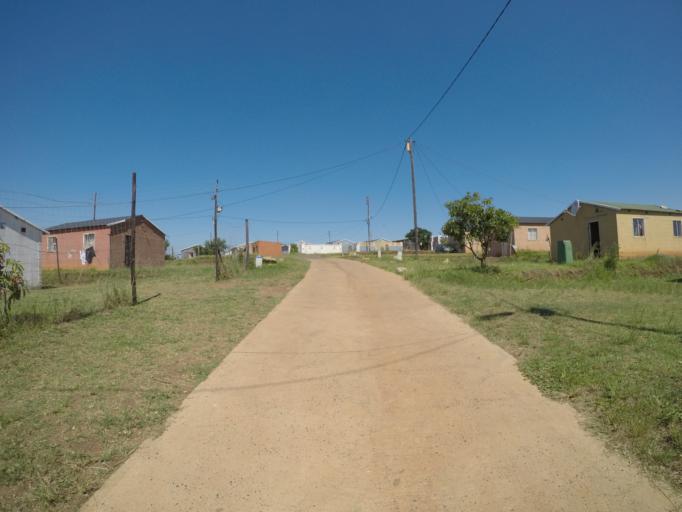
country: ZA
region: KwaZulu-Natal
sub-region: uThungulu District Municipality
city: Empangeni
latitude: -28.7679
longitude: 31.8765
